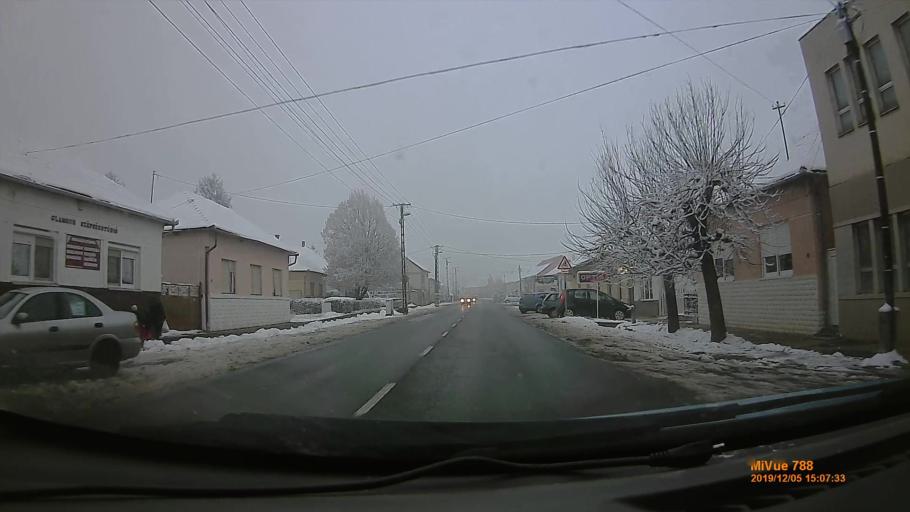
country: HU
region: Szabolcs-Szatmar-Bereg
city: Rakamaz
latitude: 48.1219
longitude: 21.4693
